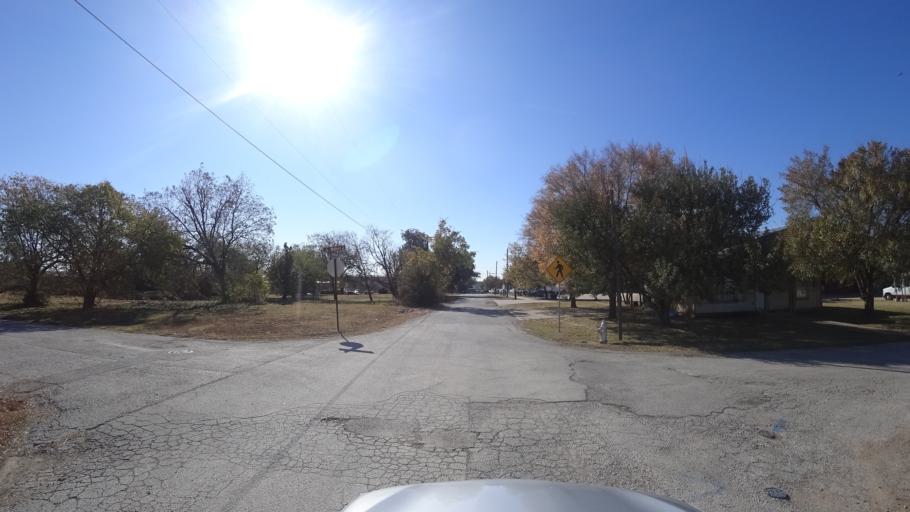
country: US
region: Texas
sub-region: Denton County
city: Lewisville
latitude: 33.0482
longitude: -96.9905
